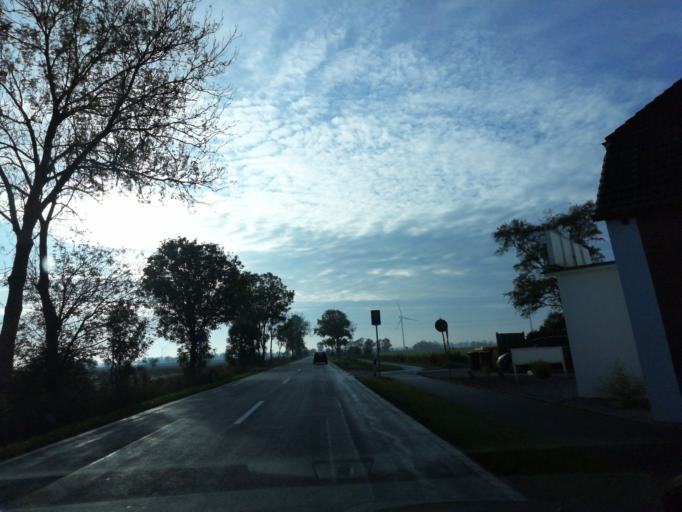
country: DE
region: Lower Saxony
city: Fedderwarden
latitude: 53.6191
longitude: 8.0358
